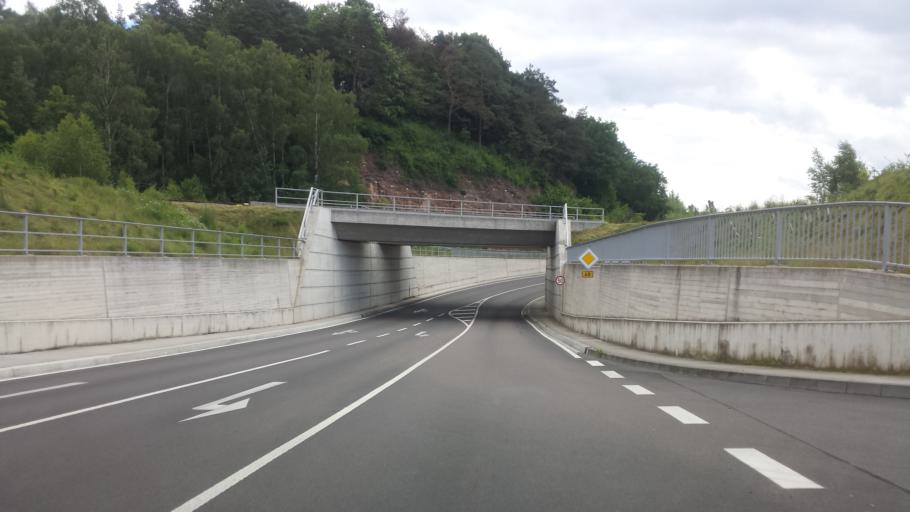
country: DE
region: Rheinland-Pfalz
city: Enkenbach-Alsenborn
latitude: 49.4918
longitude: 7.8982
